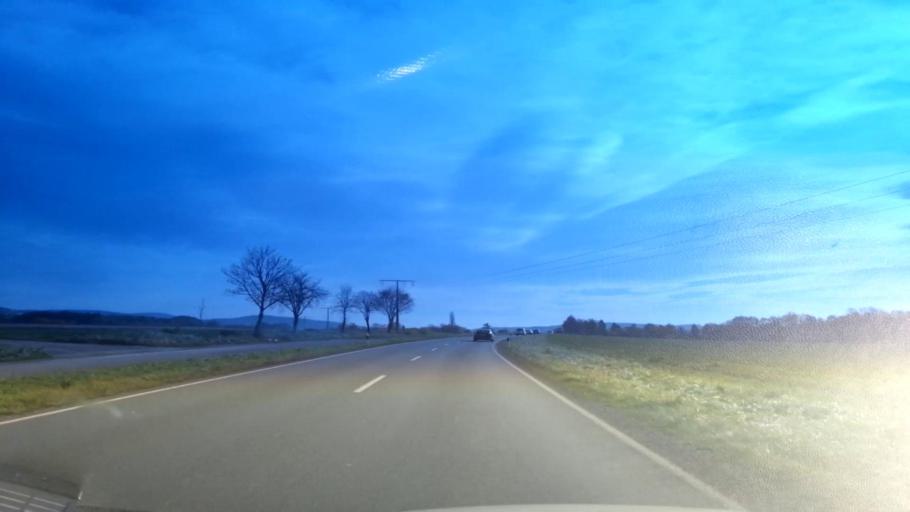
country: DE
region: Bavaria
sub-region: Upper Franconia
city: Reuth
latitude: 49.9512
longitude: 11.7104
